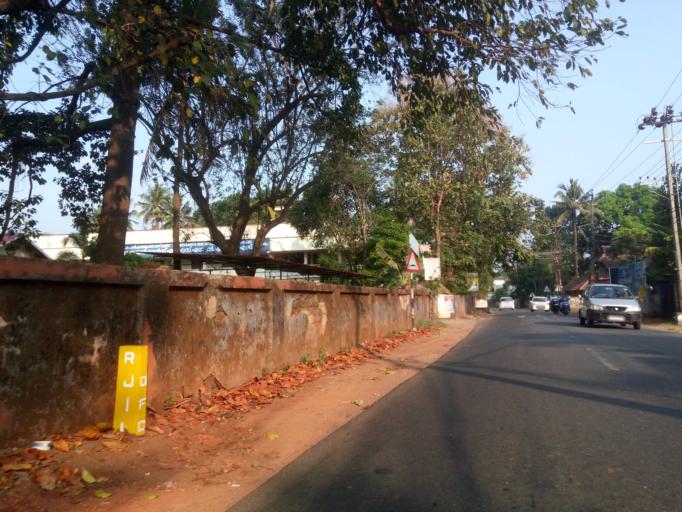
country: IN
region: Kerala
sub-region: Thrissur District
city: Irinjalakuda
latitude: 10.3428
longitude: 76.2103
